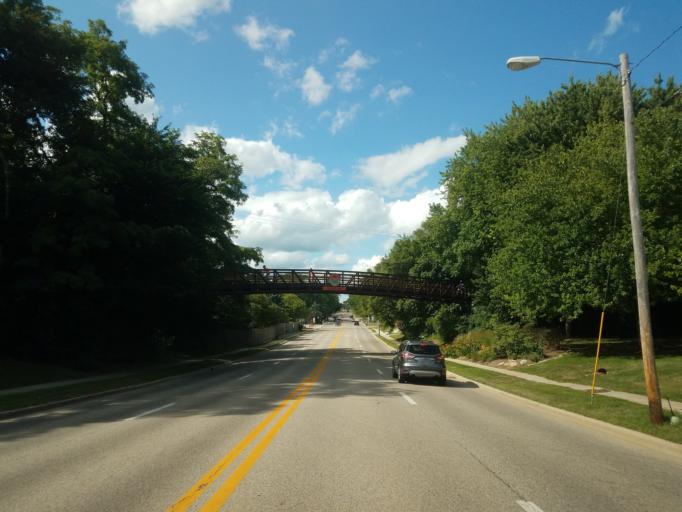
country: US
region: Illinois
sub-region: McLean County
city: Normal
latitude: 40.5020
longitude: -88.9822
